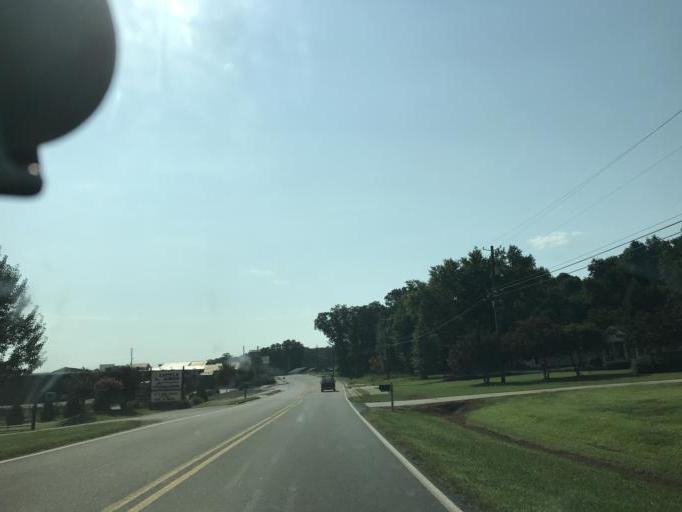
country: US
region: Georgia
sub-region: Forsyth County
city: Cumming
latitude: 34.2611
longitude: -84.1083
